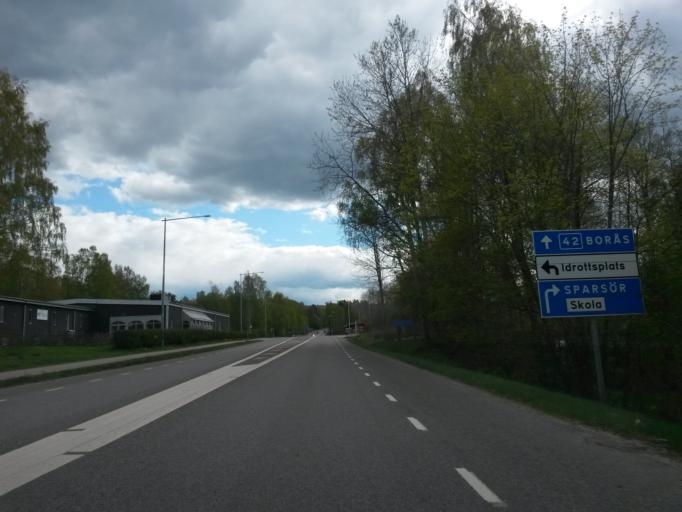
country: SE
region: Vaestra Goetaland
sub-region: Boras Kommun
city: Ganghester
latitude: 57.8058
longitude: 13.0113
